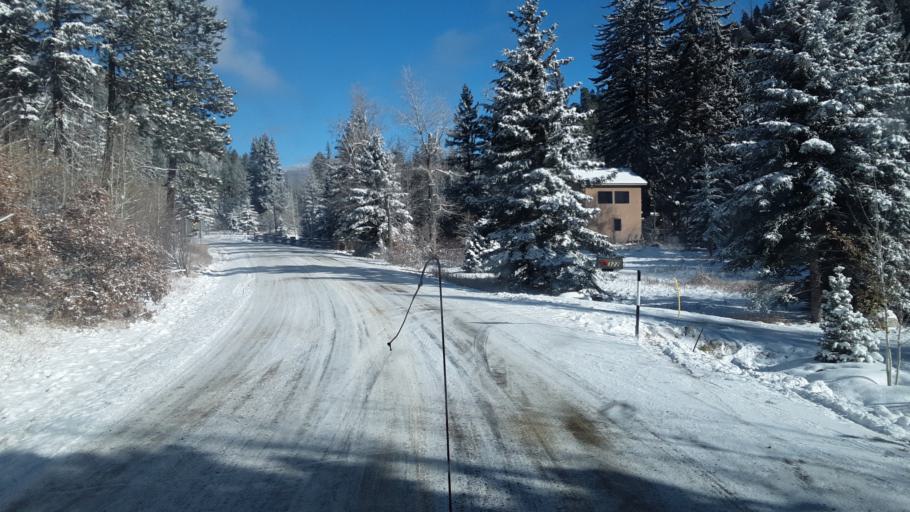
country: US
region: Colorado
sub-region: La Plata County
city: Bayfield
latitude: 37.3644
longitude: -107.6674
